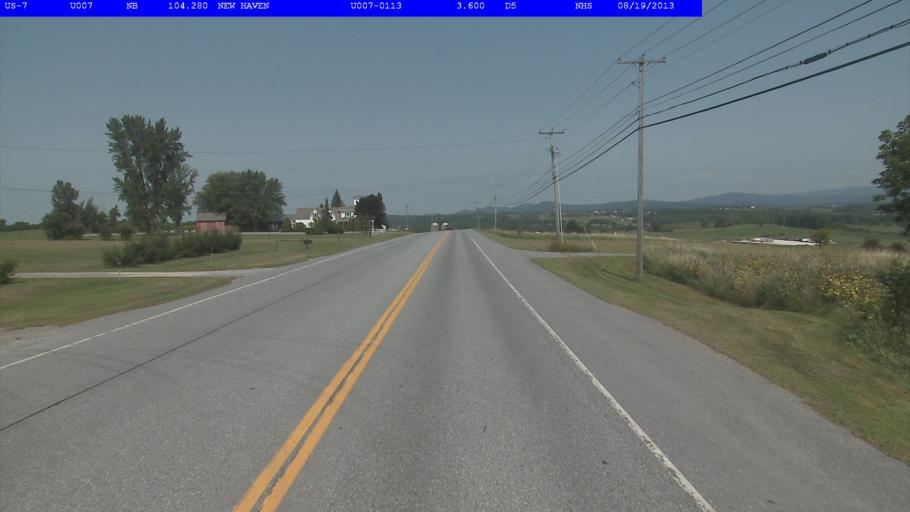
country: US
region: Vermont
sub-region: Addison County
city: Middlebury (village)
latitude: 44.0973
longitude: -73.1732
